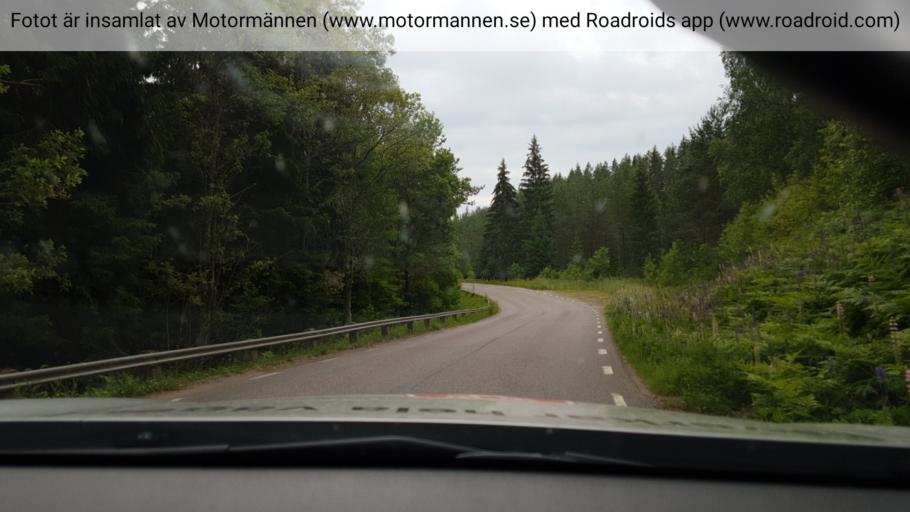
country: SE
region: Vaestra Goetaland
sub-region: Tidaholms Kommun
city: Tidaholm
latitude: 58.0831
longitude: 13.9072
